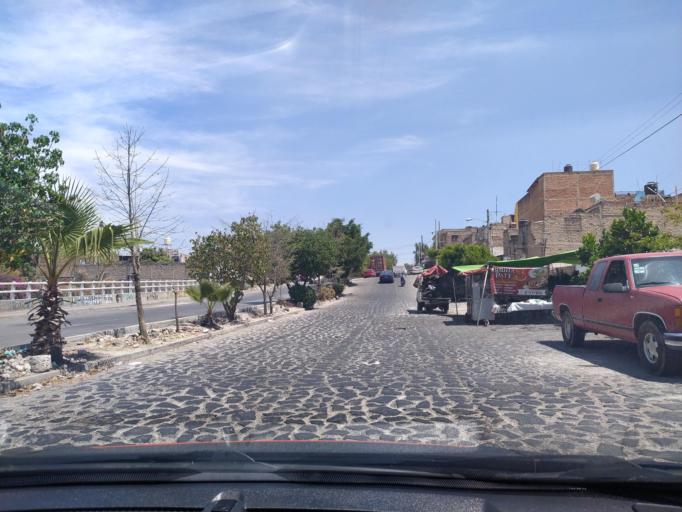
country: MX
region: Jalisco
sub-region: Tlajomulco de Zuniga
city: Altus Bosques
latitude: 20.6123
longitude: -103.3733
